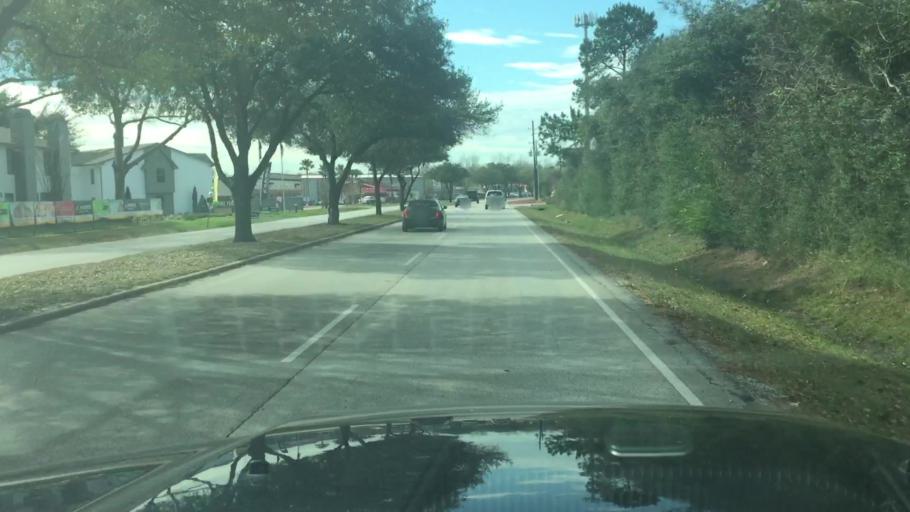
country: US
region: Texas
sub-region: Harris County
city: Oak Cliff Place
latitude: 29.8333
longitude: -95.6581
